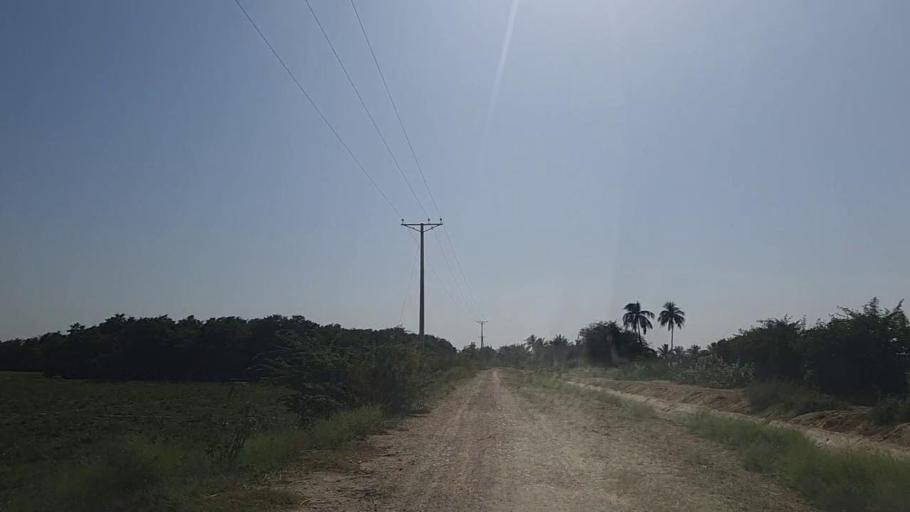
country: PK
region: Sindh
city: Thatta
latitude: 24.6303
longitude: 67.8789
